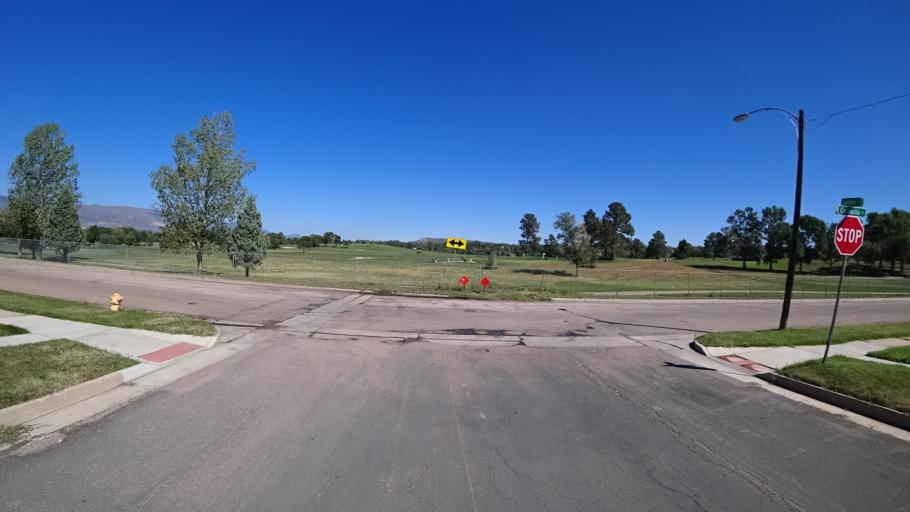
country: US
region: Colorado
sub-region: El Paso County
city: Colorado Springs
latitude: 38.8552
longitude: -104.7987
